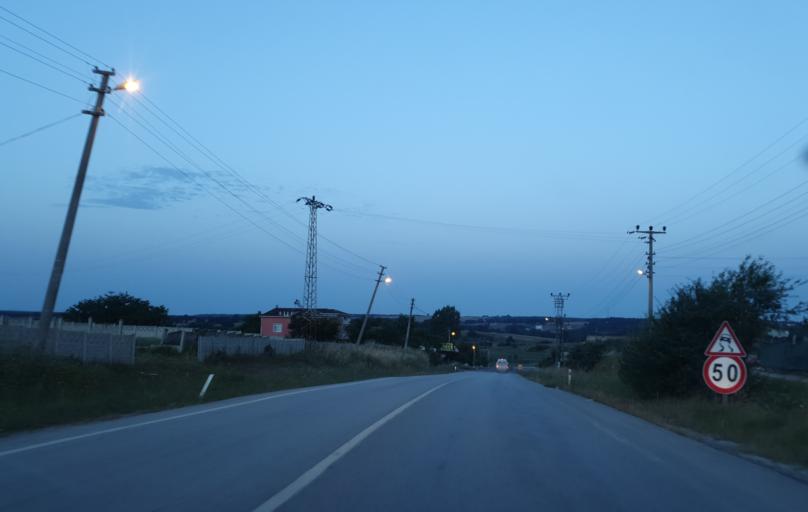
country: TR
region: Tekirdag
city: Saray
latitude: 41.3710
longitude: 27.9373
